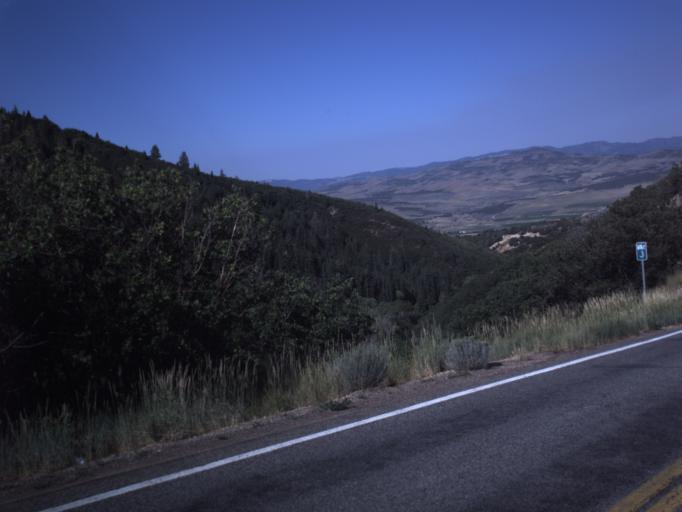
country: US
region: Utah
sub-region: Sanpete County
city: Fairview
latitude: 39.6490
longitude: -111.3920
